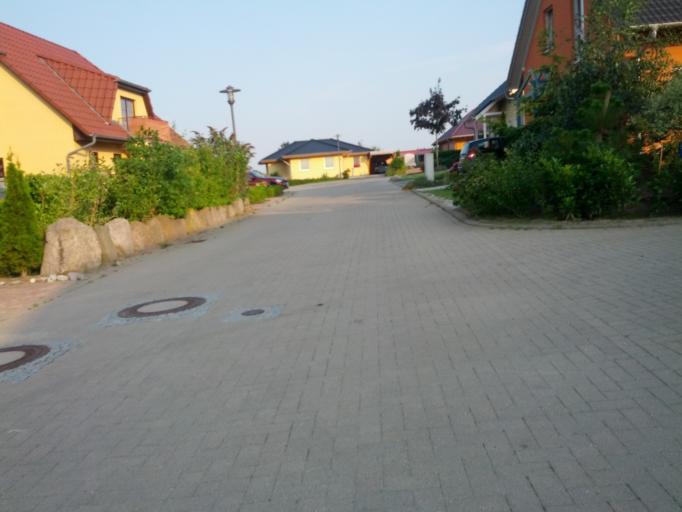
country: DE
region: Mecklenburg-Vorpommern
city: Ostseebad Kuhlungsborn
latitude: 54.1405
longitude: 11.7582
